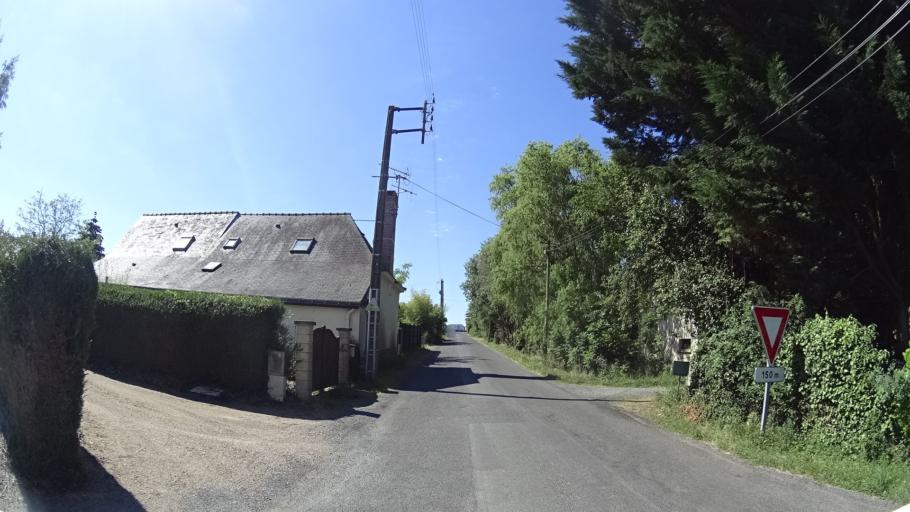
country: FR
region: Pays de la Loire
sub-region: Departement de Maine-et-Loire
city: Saint-Mathurin-sur-Loire
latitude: 47.4126
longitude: -0.3335
